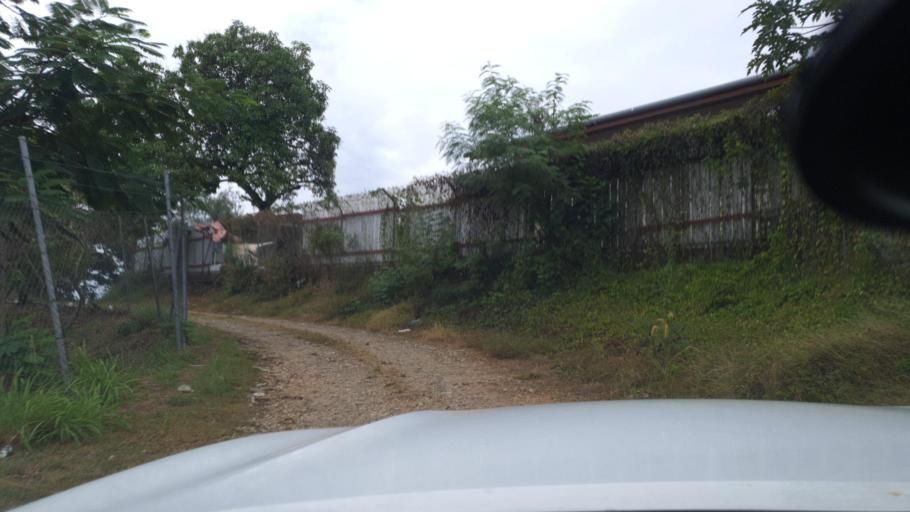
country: SB
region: Guadalcanal
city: Honiara
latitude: -9.4435
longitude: 159.9685
